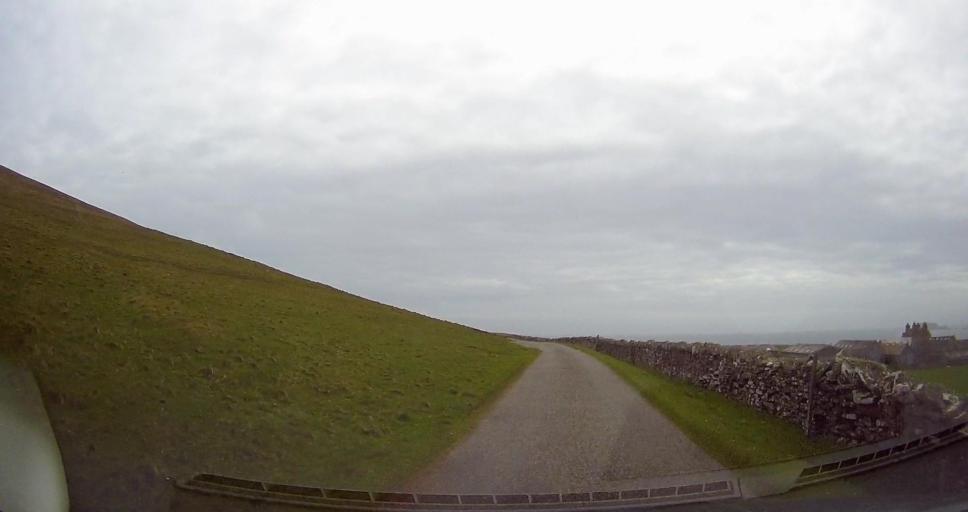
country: GB
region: Scotland
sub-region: Shetland Islands
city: Sandwick
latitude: 59.8692
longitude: -1.2790
